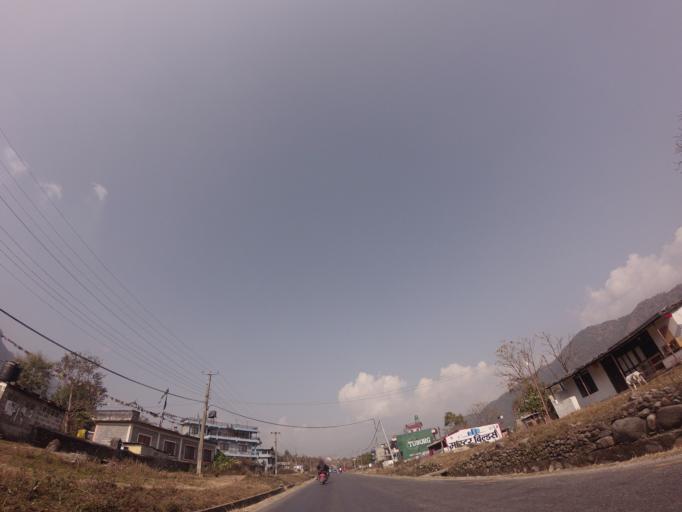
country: NP
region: Western Region
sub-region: Gandaki Zone
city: Pokhara
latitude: 28.2636
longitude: 83.9568
